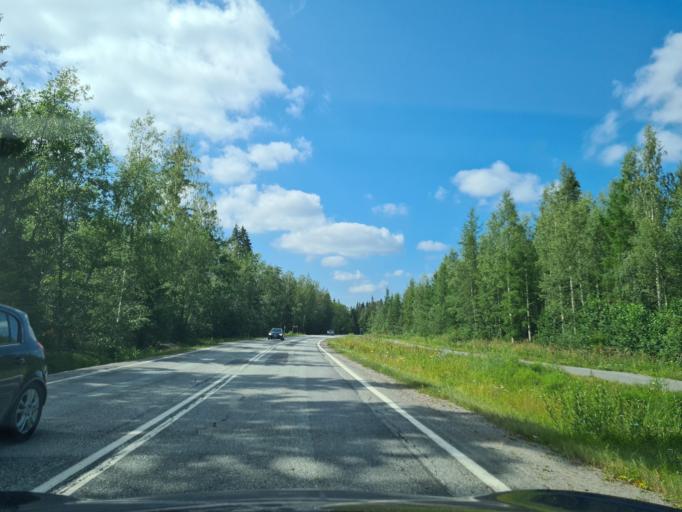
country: FI
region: Ostrobothnia
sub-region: Vaasa
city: Vaasa
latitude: 63.1948
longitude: 21.5513
